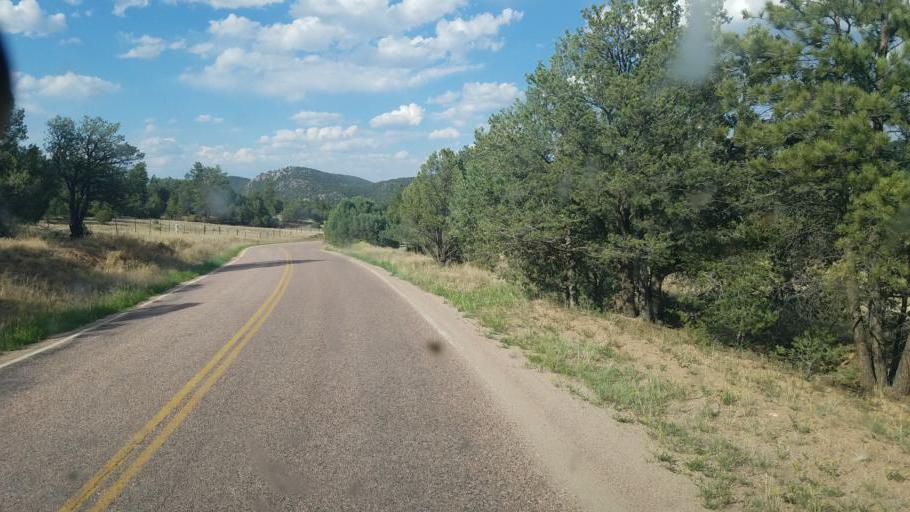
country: US
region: Colorado
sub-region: Custer County
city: Westcliffe
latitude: 38.3621
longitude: -105.4682
